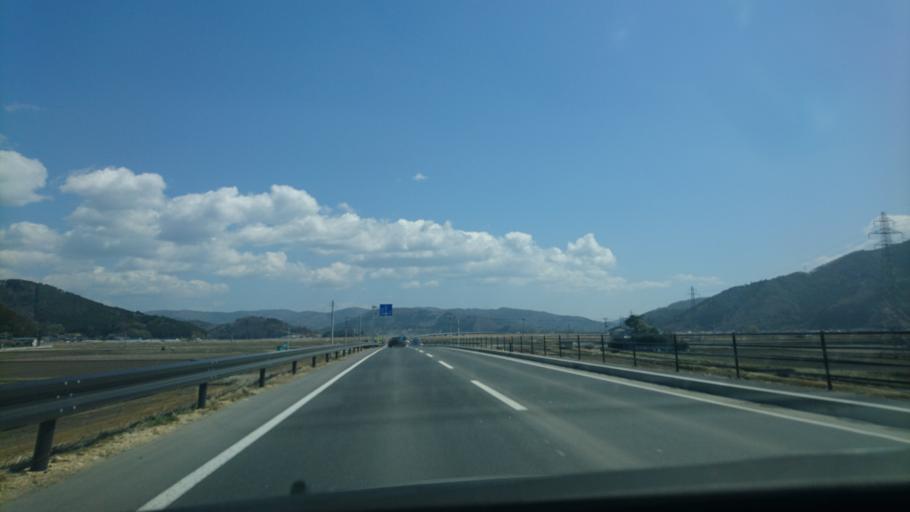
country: JP
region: Miyagi
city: Ishinomaki
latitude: 38.4503
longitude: 141.3220
